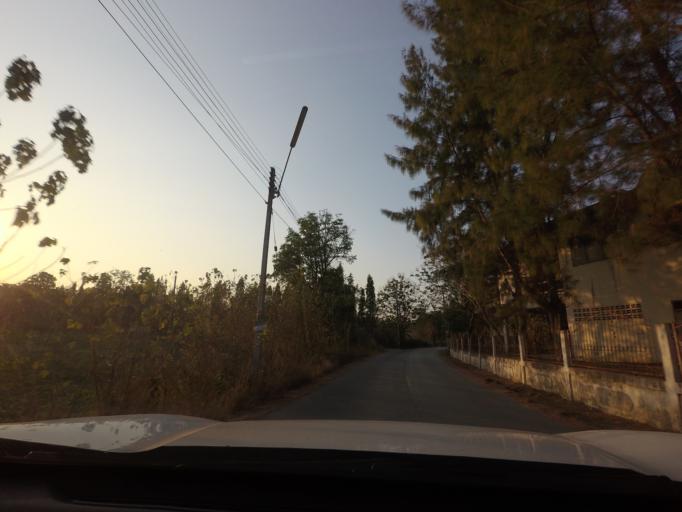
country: TH
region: Nakhon Ratchasima
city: Pak Chong
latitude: 14.6462
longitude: 101.4208
